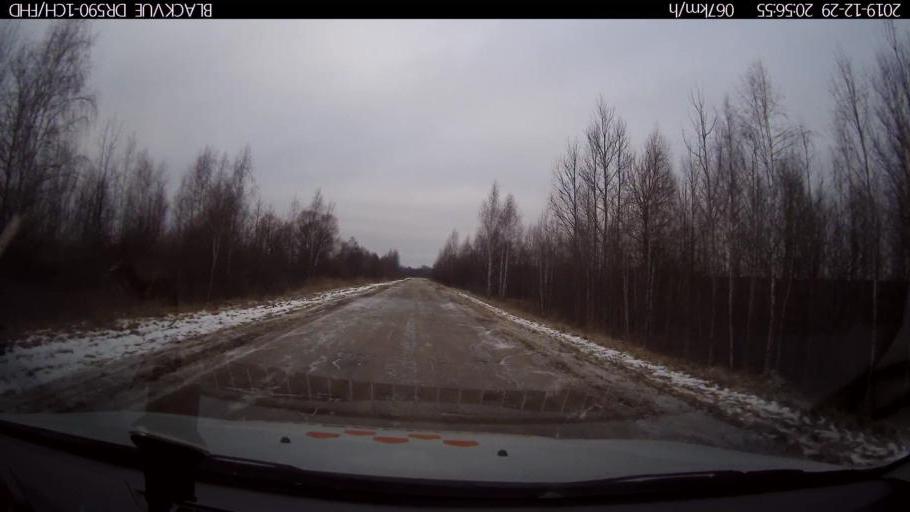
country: RU
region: Nizjnij Novgorod
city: Afonino
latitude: 56.1565
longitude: 43.9960
